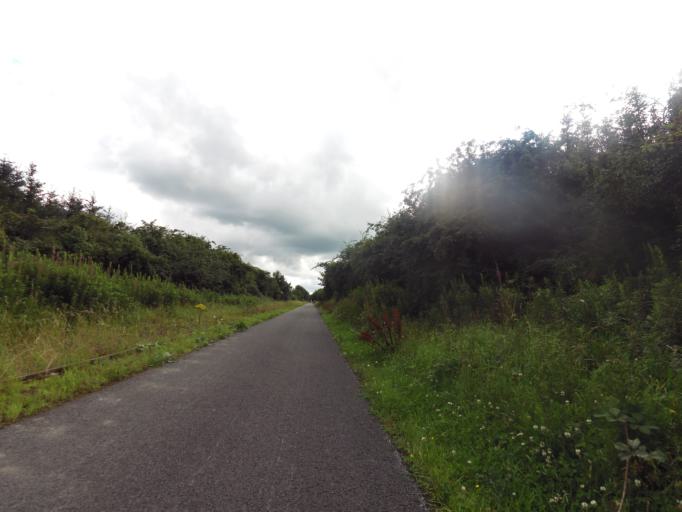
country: IE
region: Leinster
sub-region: An Iarmhi
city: An Muileann gCearr
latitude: 53.4949
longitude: -7.4461
